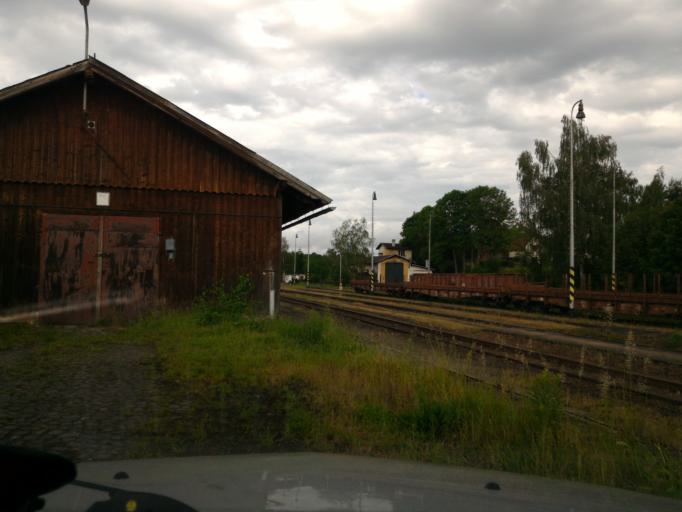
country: CZ
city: Jablonne v Podjestedi
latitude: 50.7691
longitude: 14.7568
